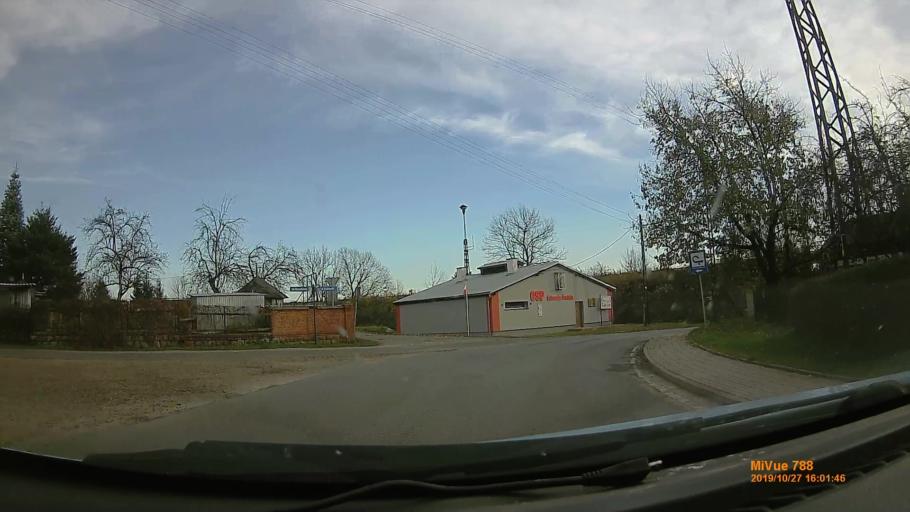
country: PL
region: Lower Silesian Voivodeship
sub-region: Powiat klodzki
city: Nowa Ruda
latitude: 50.5226
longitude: 16.5092
